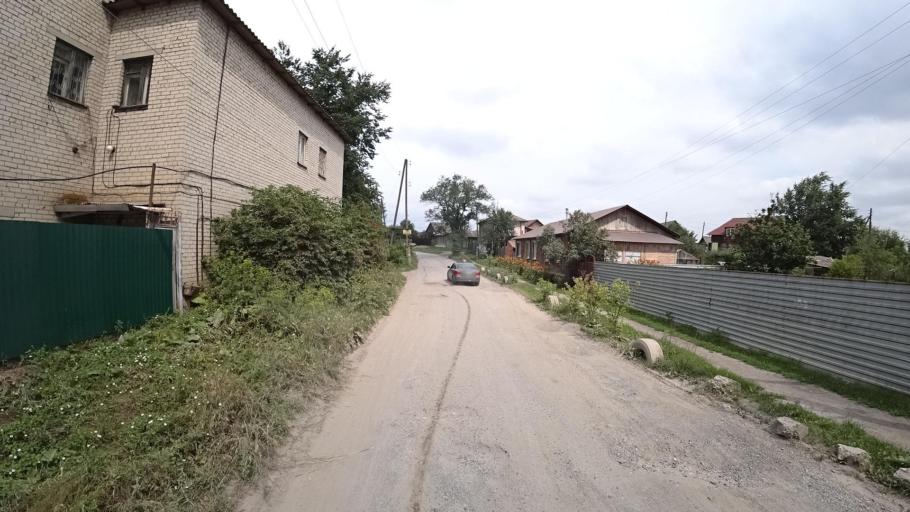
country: RU
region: Sverdlovsk
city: Kamyshlov
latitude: 56.8469
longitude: 62.6815
